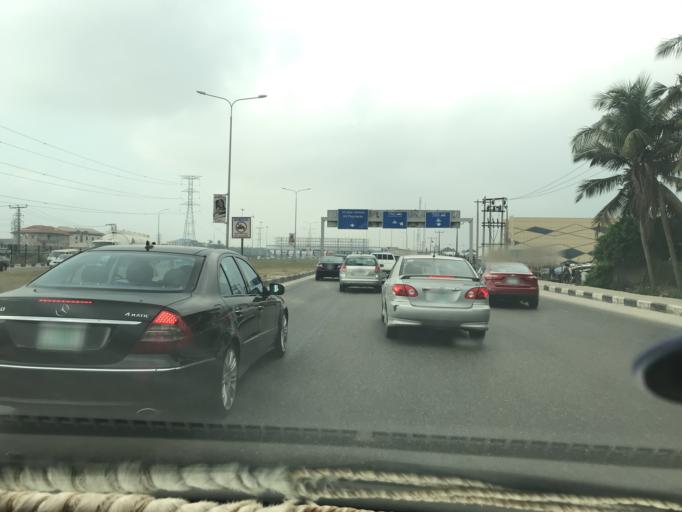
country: NG
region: Lagos
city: Ikoyi
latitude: 6.4466
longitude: 3.5433
